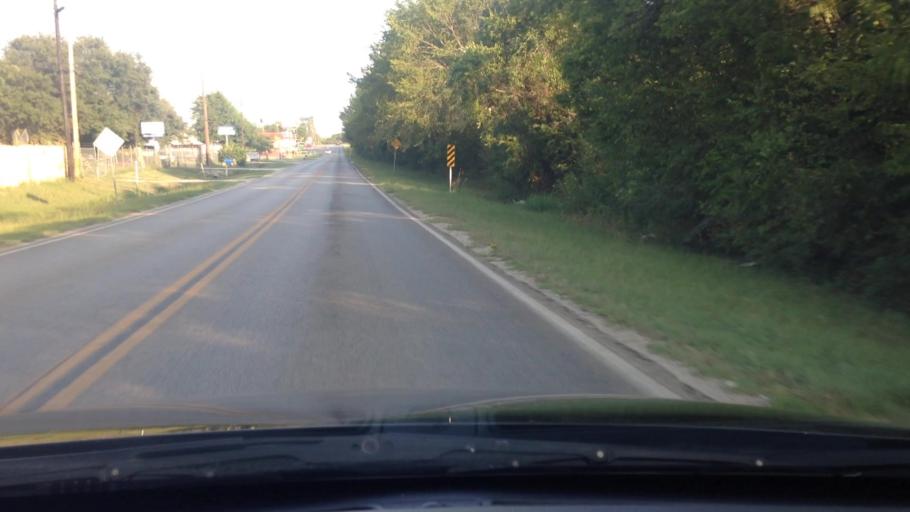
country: US
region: Texas
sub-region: Tarrant County
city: Rendon
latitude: 32.5876
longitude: -97.2484
